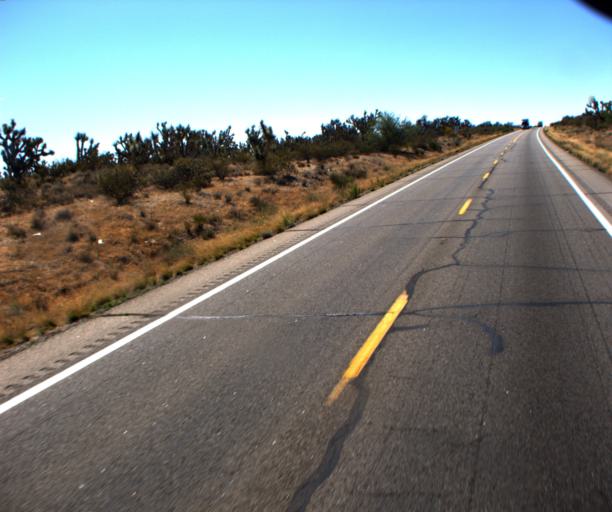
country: US
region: Arizona
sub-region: Yavapai County
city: Congress
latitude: 34.2676
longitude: -113.0923
